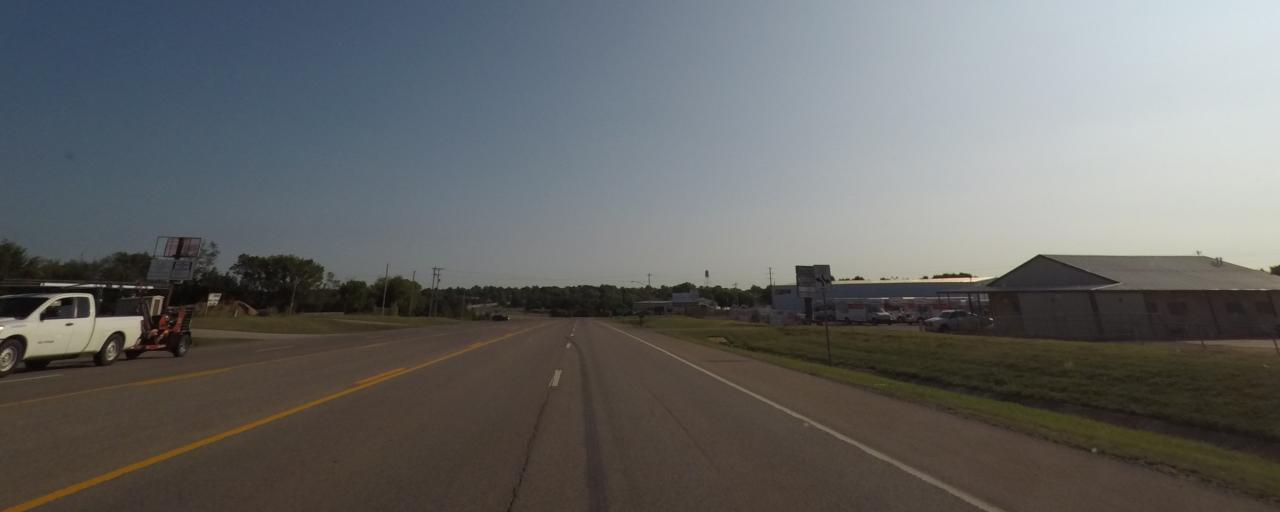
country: US
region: Oklahoma
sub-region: McClain County
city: Blanchard
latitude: 35.1297
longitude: -97.6679
